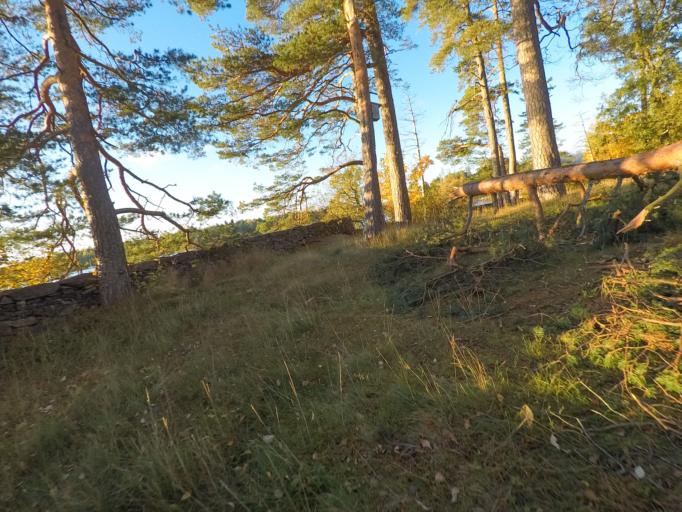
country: FI
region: Uusimaa
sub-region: Helsinki
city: Vantaa
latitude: 60.1550
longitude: 25.0811
